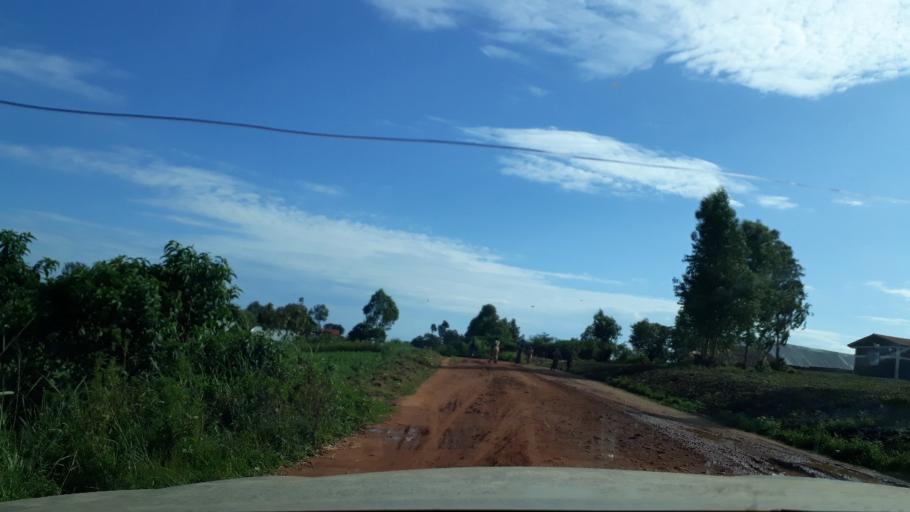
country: UG
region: Northern Region
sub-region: Zombo District
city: Paidha
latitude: 2.3455
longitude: 31.0277
